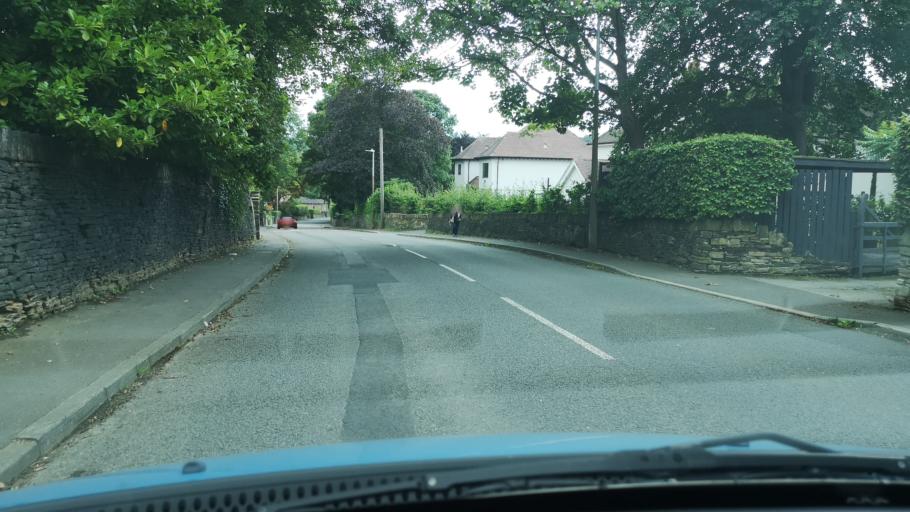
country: GB
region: England
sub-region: Kirklees
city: Mirfield
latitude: 53.6781
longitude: -1.6799
